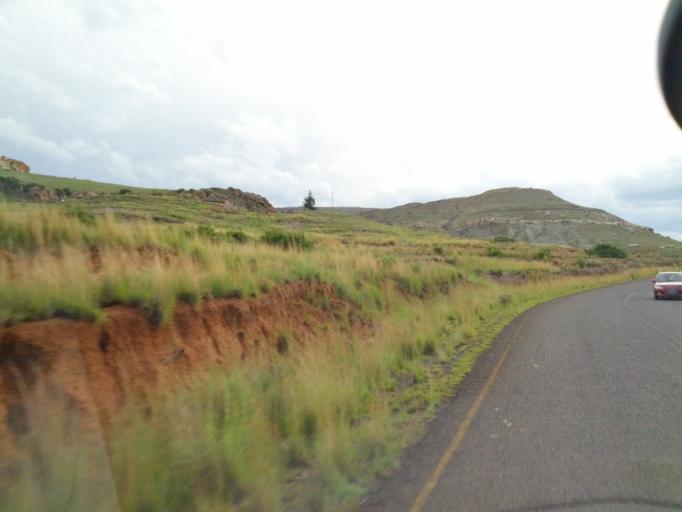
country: LS
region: Qacha's Nek
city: Qacha's Nek
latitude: -30.0728
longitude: 28.5653
